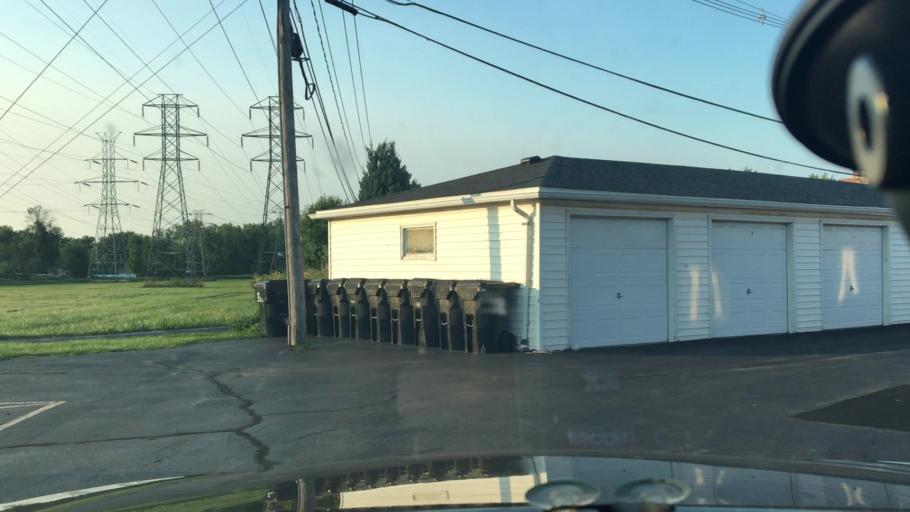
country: US
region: New York
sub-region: Erie County
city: Tonawanda
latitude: 43.0047
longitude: -78.8526
